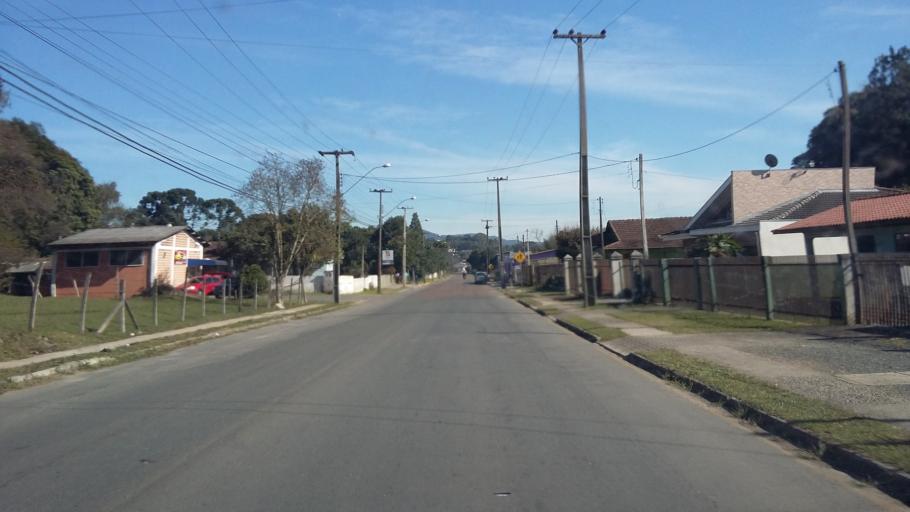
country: BR
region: Parana
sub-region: Campo Largo
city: Campo Largo
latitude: -25.4683
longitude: -49.5672
